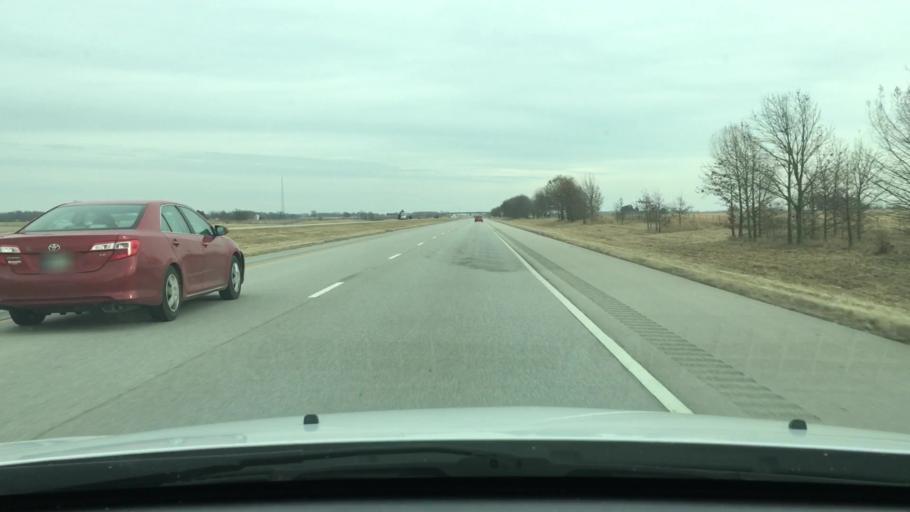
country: US
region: Illinois
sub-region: Sangamon County
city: New Berlin
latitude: 39.7367
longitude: -90.0040
